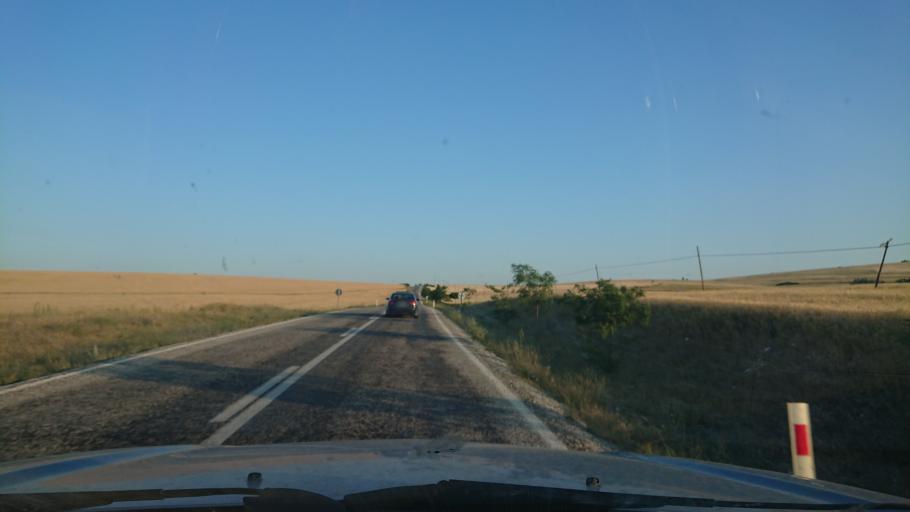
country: TR
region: Aksaray
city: Sariyahsi
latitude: 38.9321
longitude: 33.8336
